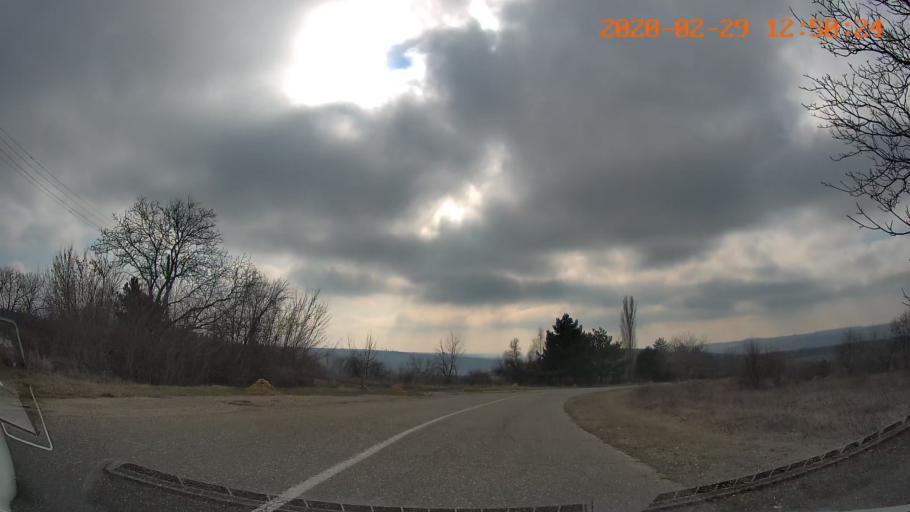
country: MD
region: Telenesti
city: Camenca
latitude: 48.1245
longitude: 28.7395
